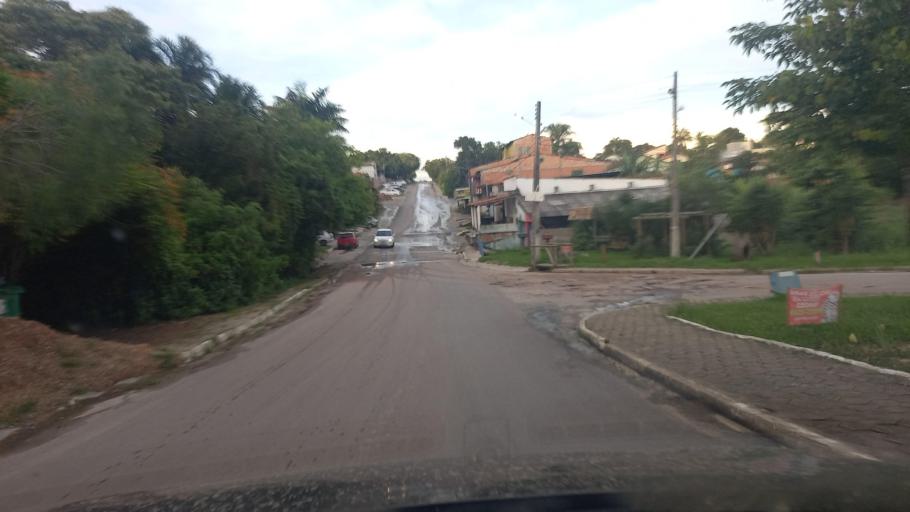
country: BR
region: Goias
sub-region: Cavalcante
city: Cavalcante
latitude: -13.7955
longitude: -47.4606
